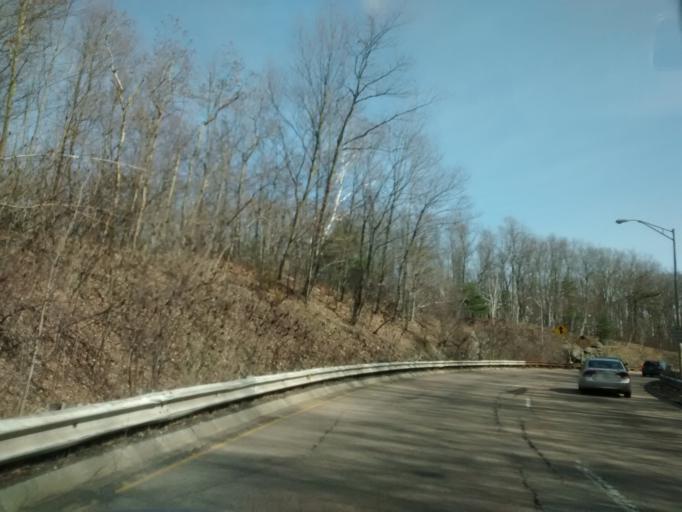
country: US
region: Massachusetts
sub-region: Worcester County
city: Auburn
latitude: 42.1909
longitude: -71.8548
